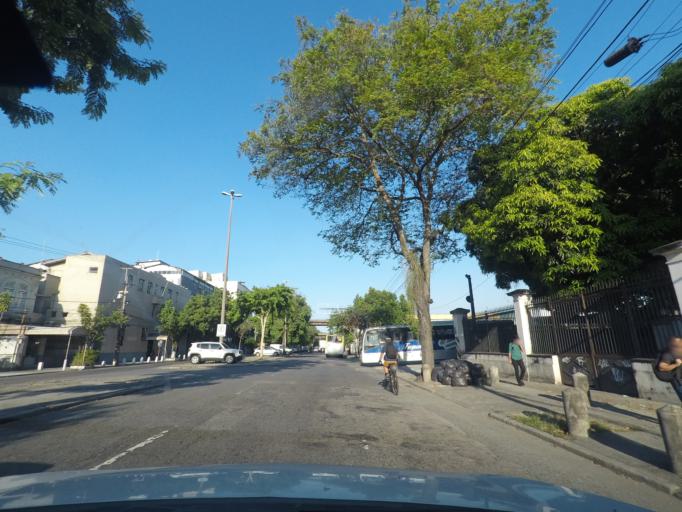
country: BR
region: Rio de Janeiro
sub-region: Rio De Janeiro
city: Rio de Janeiro
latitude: -22.9044
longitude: -43.2170
